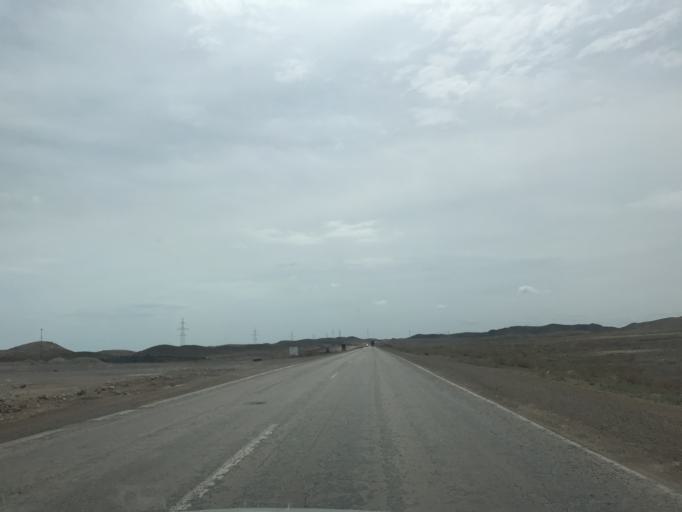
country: KZ
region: Zhambyl
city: Mynaral
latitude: 45.3648
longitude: 73.6662
